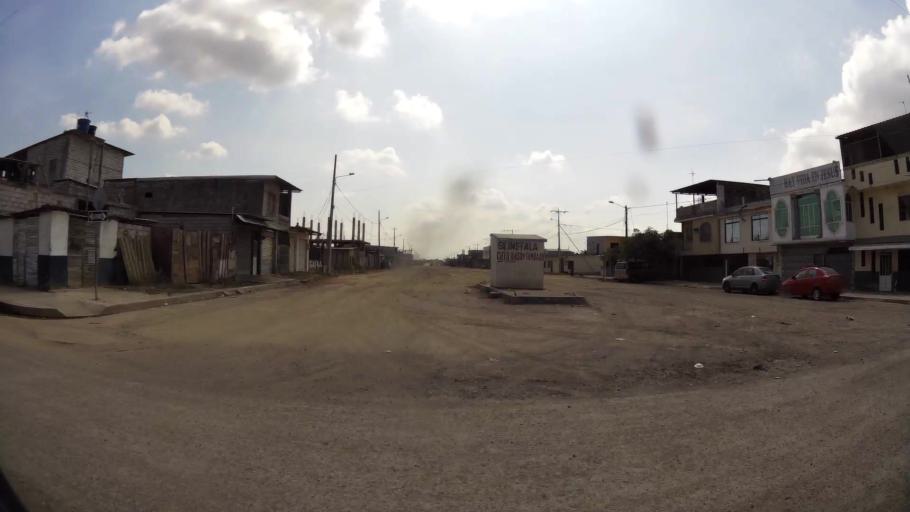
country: EC
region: Guayas
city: Eloy Alfaro
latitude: -2.1674
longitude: -79.8312
